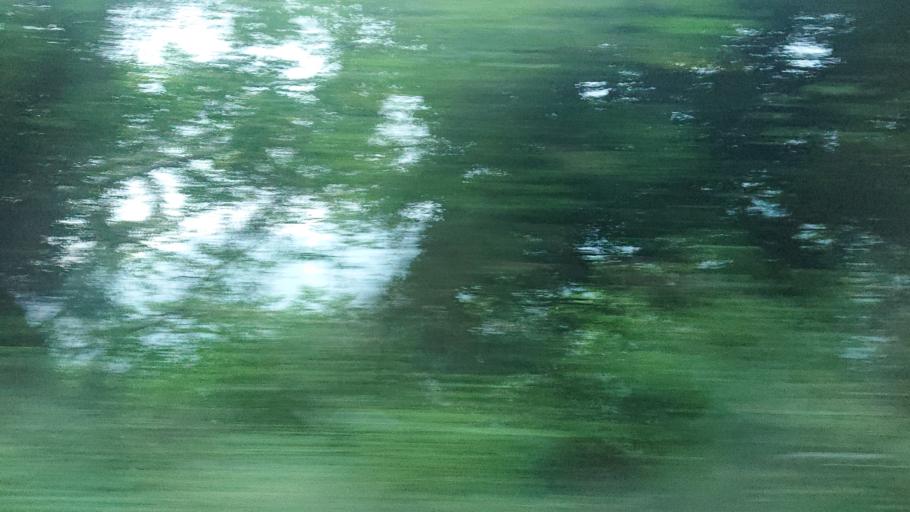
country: TW
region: Taiwan
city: Lugu
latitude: 23.5938
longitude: 120.7238
